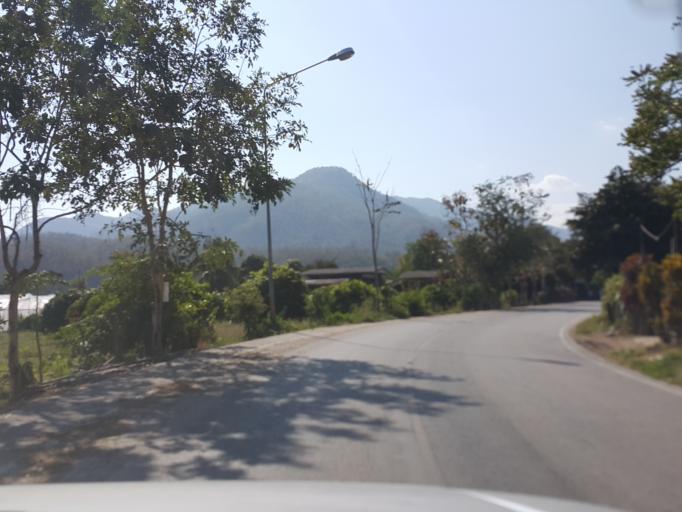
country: TH
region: Chiang Mai
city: Mae Wang
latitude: 18.6183
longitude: 98.7622
